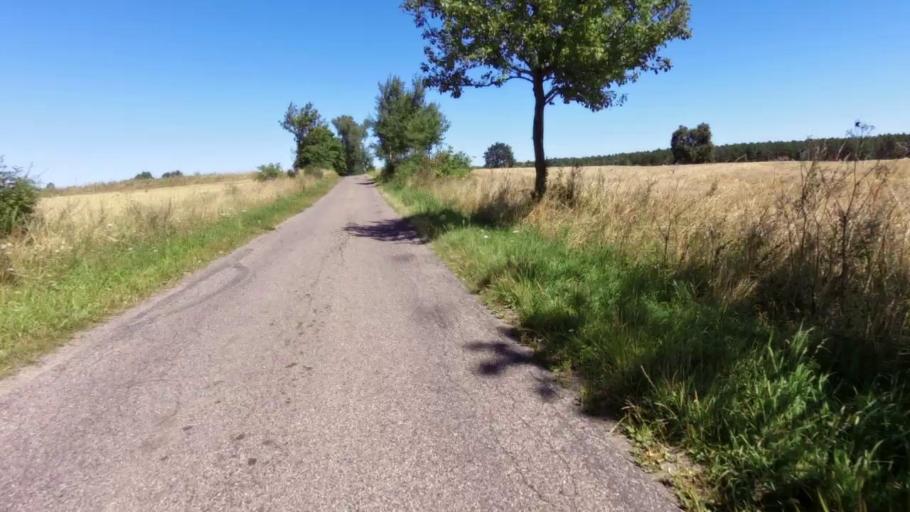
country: PL
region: West Pomeranian Voivodeship
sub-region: Powiat szczecinecki
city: Lubowo
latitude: 53.5664
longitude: 16.3583
